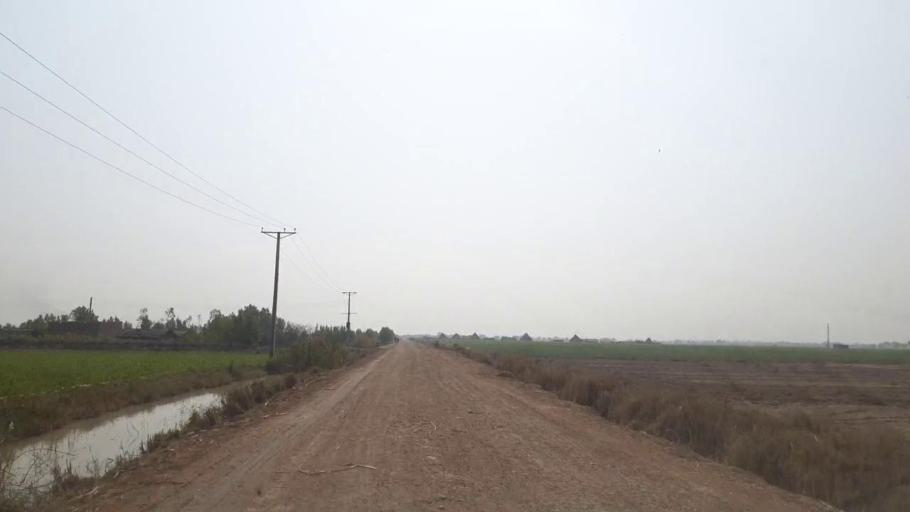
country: PK
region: Sindh
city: Mirpur Khas
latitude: 25.5448
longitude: 69.0601
